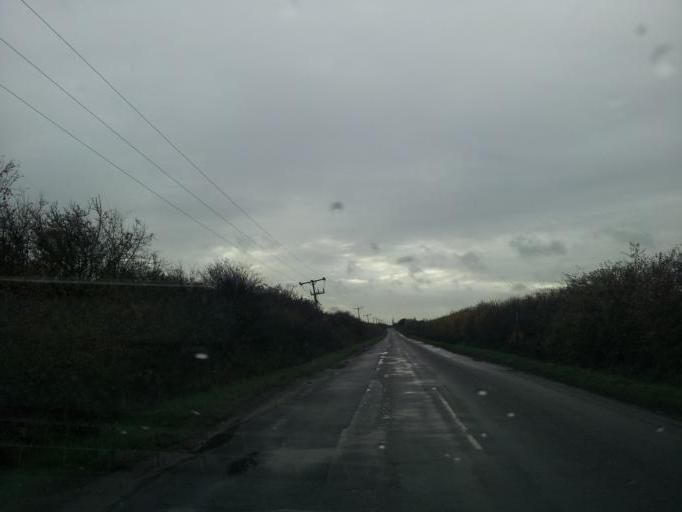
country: GB
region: England
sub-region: Nottinghamshire
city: Newark on Trent
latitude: 53.0427
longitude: -0.7970
